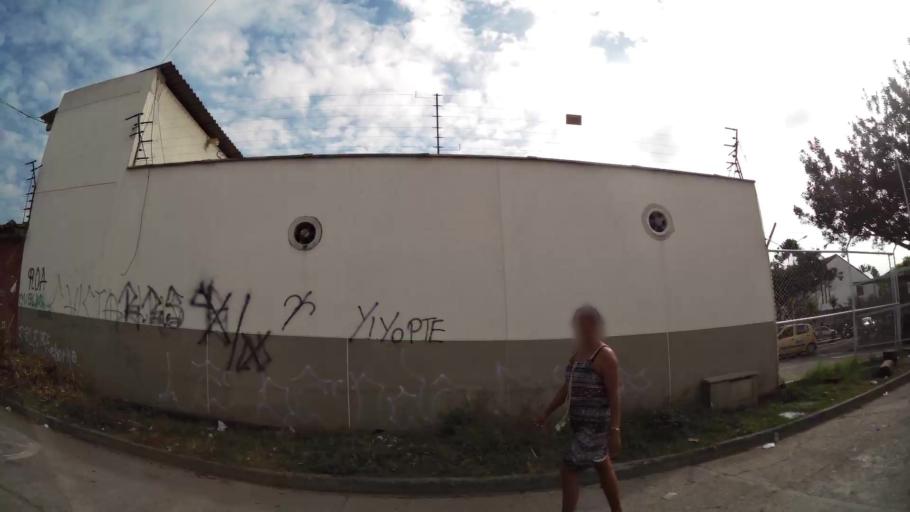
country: CO
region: Valle del Cauca
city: Cali
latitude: 3.4829
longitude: -76.4921
